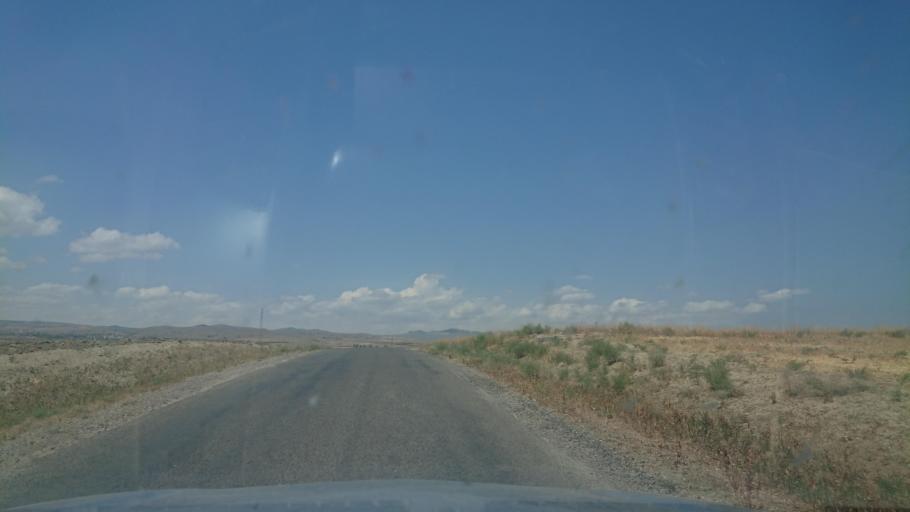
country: TR
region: Aksaray
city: Sariyahsi
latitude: 39.0025
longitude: 33.8945
